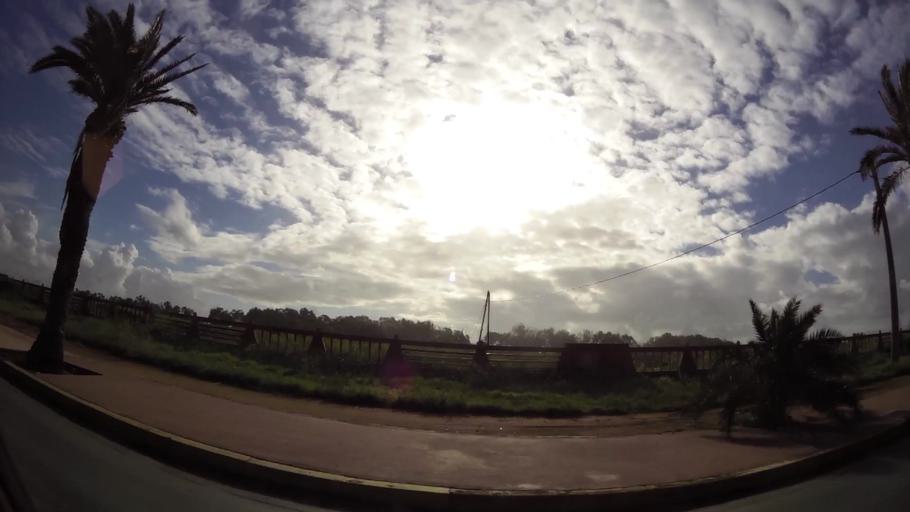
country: MA
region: Grand Casablanca
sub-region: Mohammedia
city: Mohammedia
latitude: 33.7054
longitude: -7.4011
